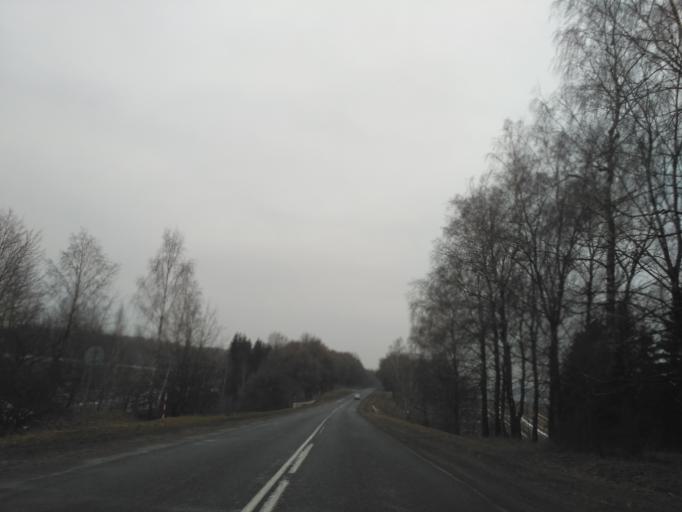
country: BY
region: Minsk
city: Snow
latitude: 53.2412
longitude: 26.2474
